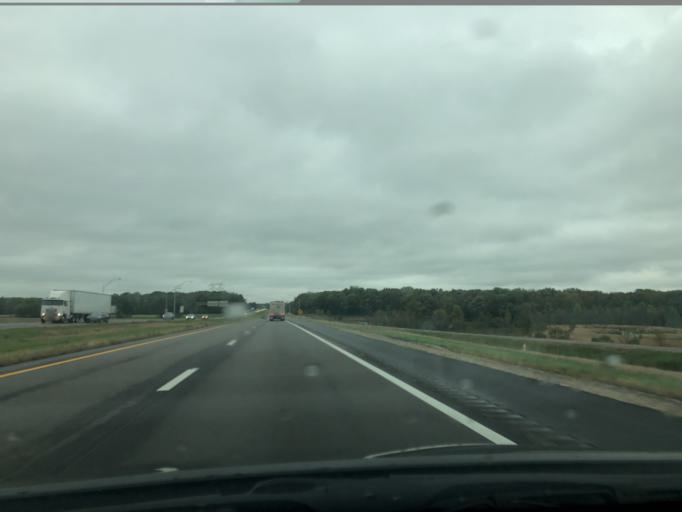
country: US
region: Ohio
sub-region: Union County
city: Marysville
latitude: 40.2390
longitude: -83.4099
